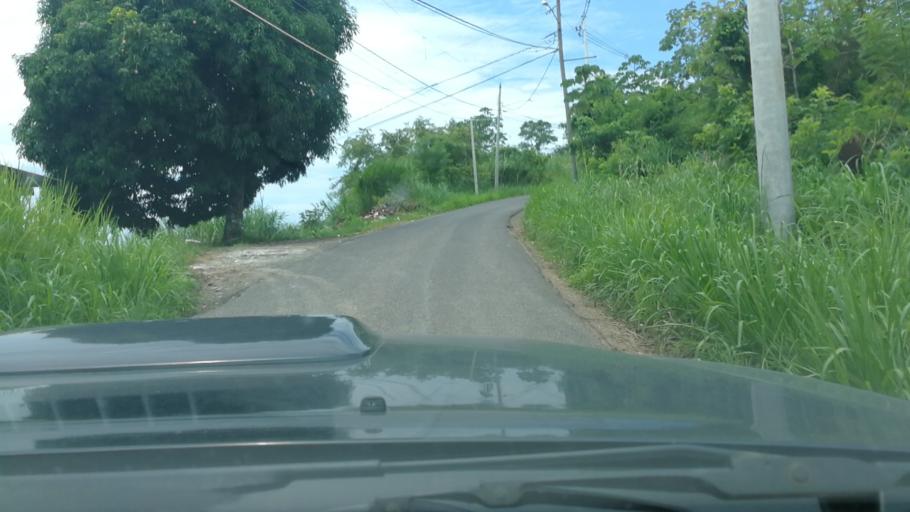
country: PA
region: Panama
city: San Miguelito
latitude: 9.1064
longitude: -79.4549
